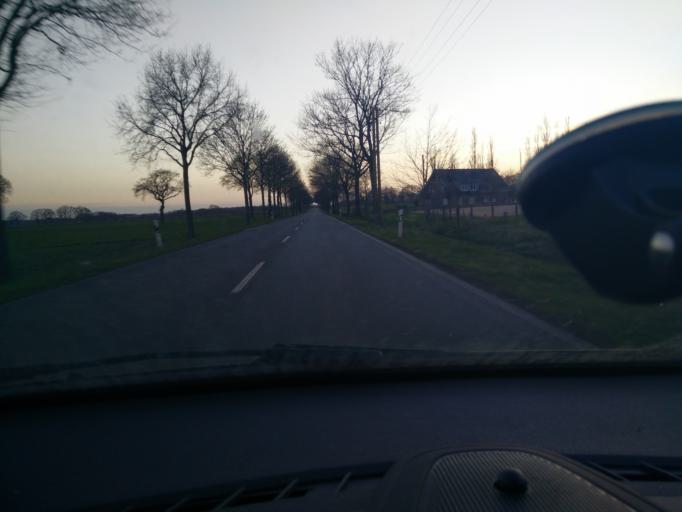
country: DE
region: North Rhine-Westphalia
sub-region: Regierungsbezirk Munster
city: Rhede
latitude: 51.7462
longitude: 6.7399
